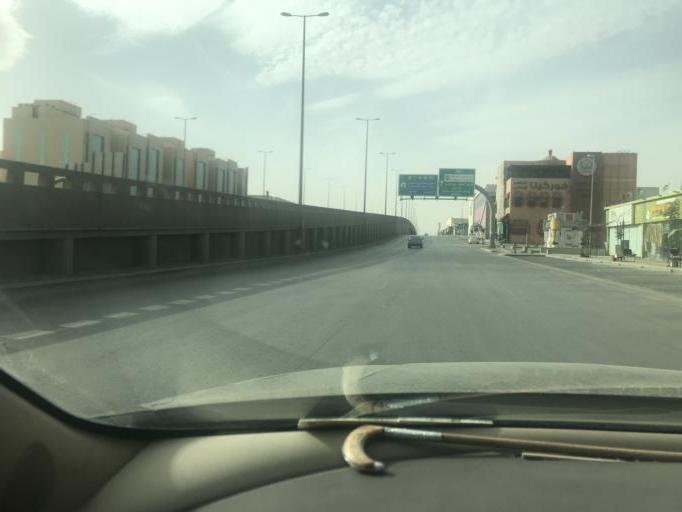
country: SA
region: Ar Riyad
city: Riyadh
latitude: 24.7722
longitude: 46.6675
